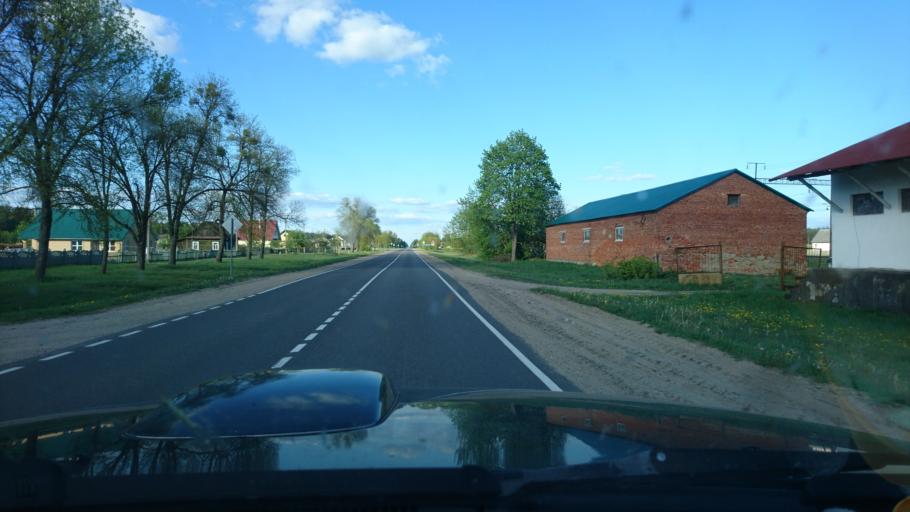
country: BY
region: Brest
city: Nyakhachava
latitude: 52.6473
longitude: 25.2123
